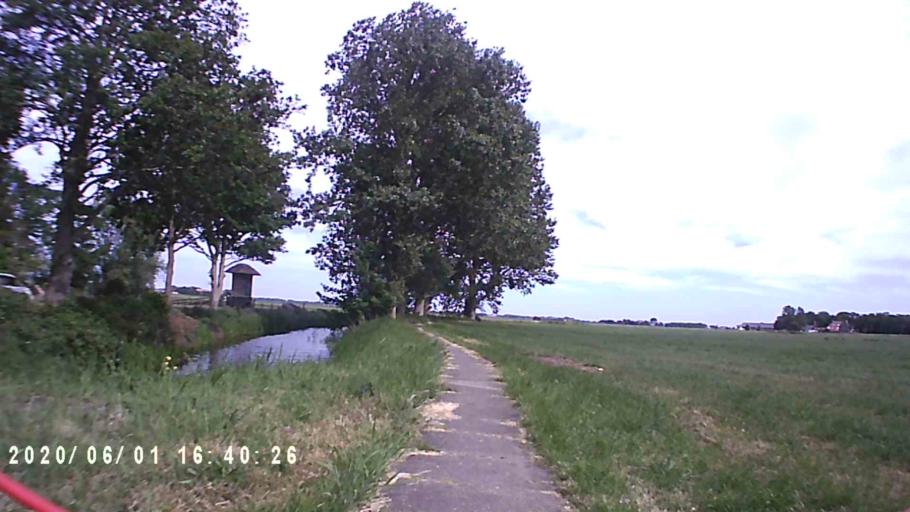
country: NL
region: Friesland
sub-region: Gemeente Leeuwarden
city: Camminghaburen
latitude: 53.1865
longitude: 5.8765
